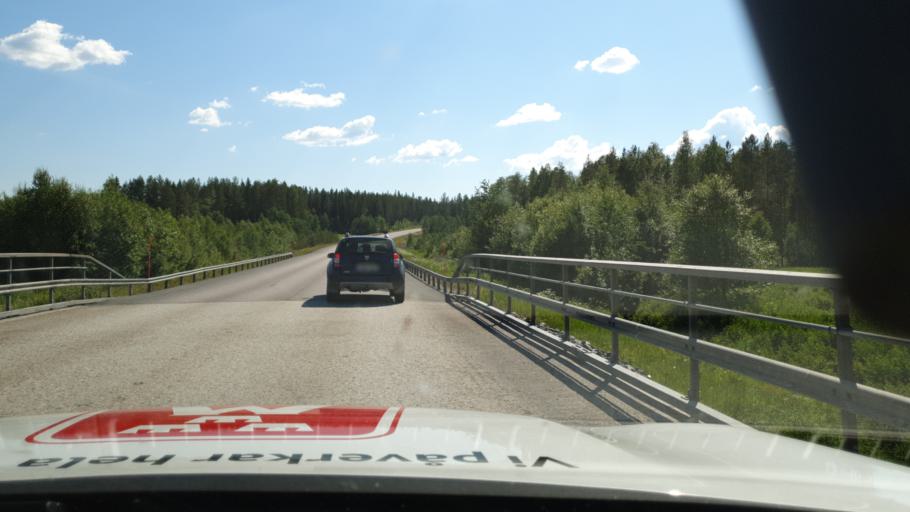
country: SE
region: Vaesterbotten
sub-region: Skelleftea Kommun
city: Viken
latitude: 64.5760
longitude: 20.9145
